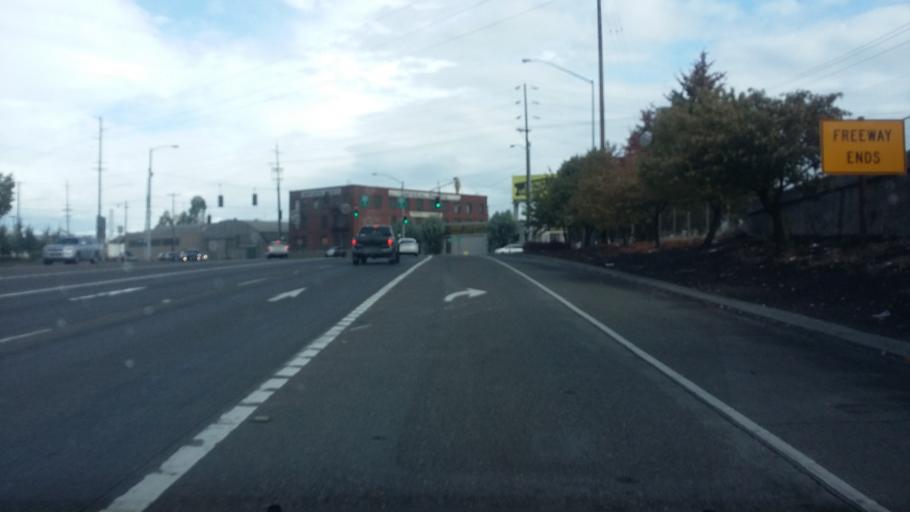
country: US
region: Oregon
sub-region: Multnomah County
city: Portland
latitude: 45.5400
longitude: -122.6983
